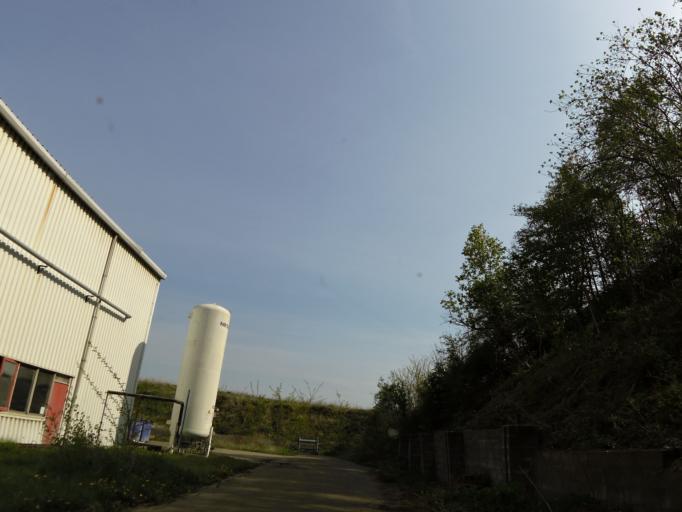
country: NL
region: Limburg
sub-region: Gemeente Brunssum
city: Brunssum
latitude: 50.9413
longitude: 5.9966
